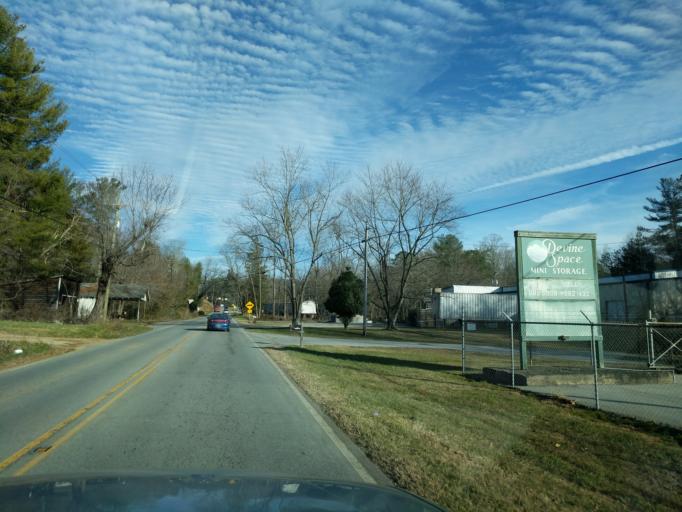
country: US
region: North Carolina
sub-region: Henderson County
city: Edneyville
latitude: 35.3894
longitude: -82.3497
